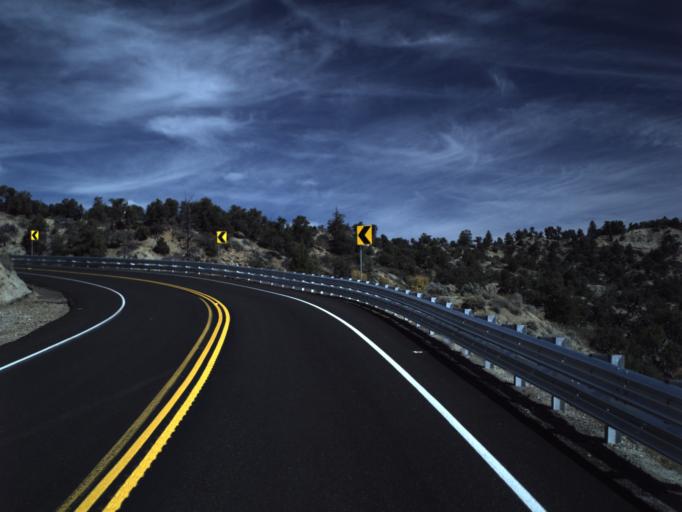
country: US
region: Utah
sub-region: Garfield County
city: Panguitch
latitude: 37.6367
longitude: -111.8421
